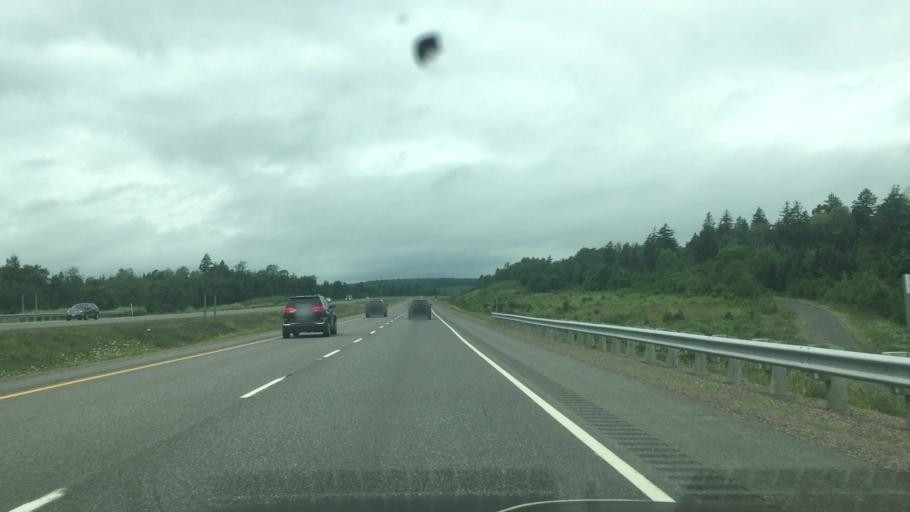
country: CA
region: Nova Scotia
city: Oxford
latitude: 45.4528
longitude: -63.6289
